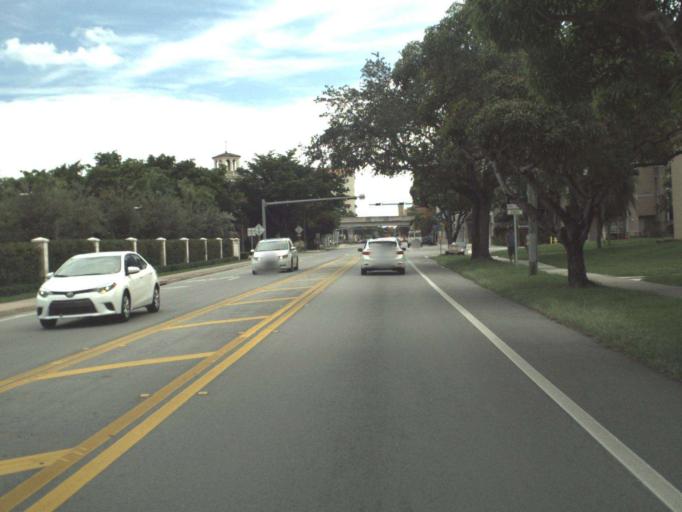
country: US
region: Florida
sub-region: Miami-Dade County
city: South Miami
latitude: 25.7106
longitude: -80.2857
